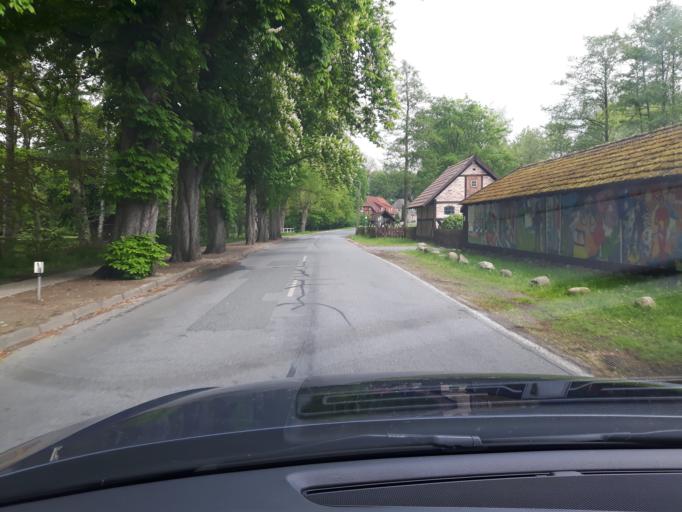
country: DE
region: Mecklenburg-Vorpommern
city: Bad Sulze
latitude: 54.1128
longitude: 12.6619
